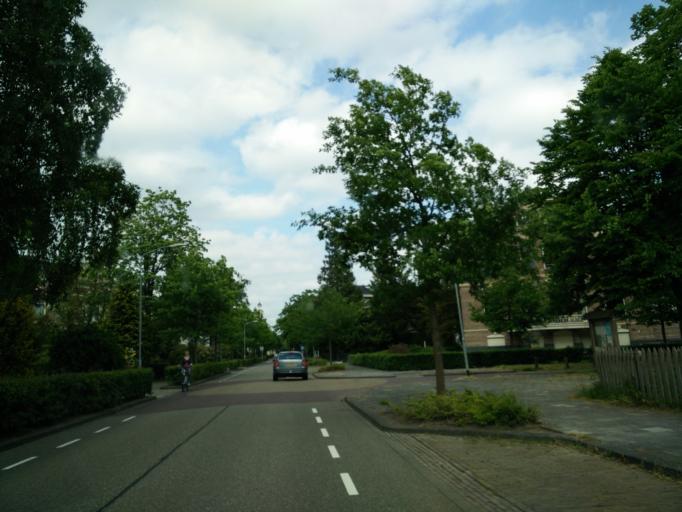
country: NL
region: Drenthe
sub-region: Gemeente Assen
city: Assen
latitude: 52.9910
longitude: 6.5562
